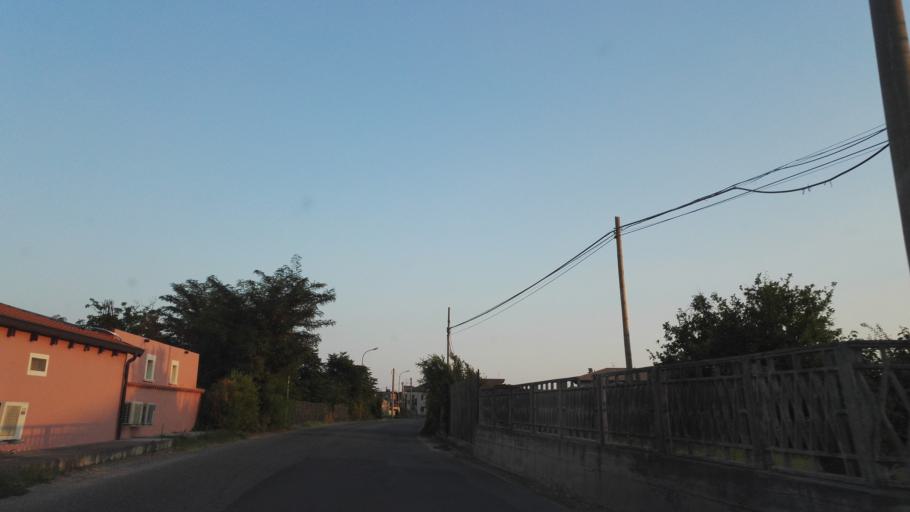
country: IT
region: Calabria
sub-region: Provincia di Reggio Calabria
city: Caulonia Marina
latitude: 38.3565
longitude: 16.4699
